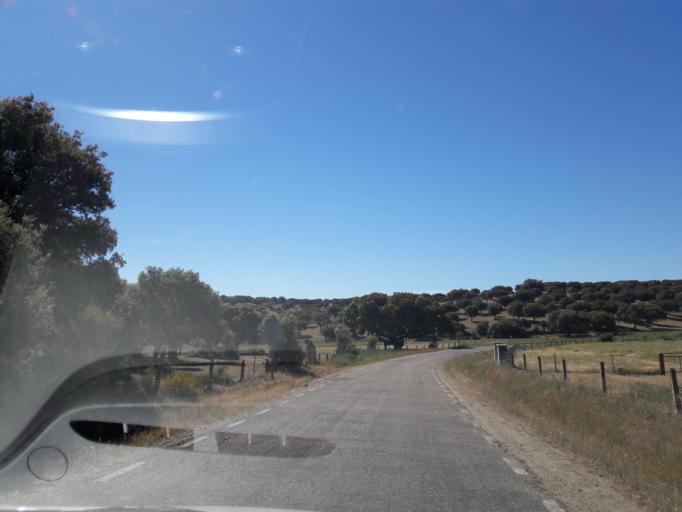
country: ES
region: Castille and Leon
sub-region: Provincia de Salamanca
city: Vega de Tirados
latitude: 41.0601
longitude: -5.8917
